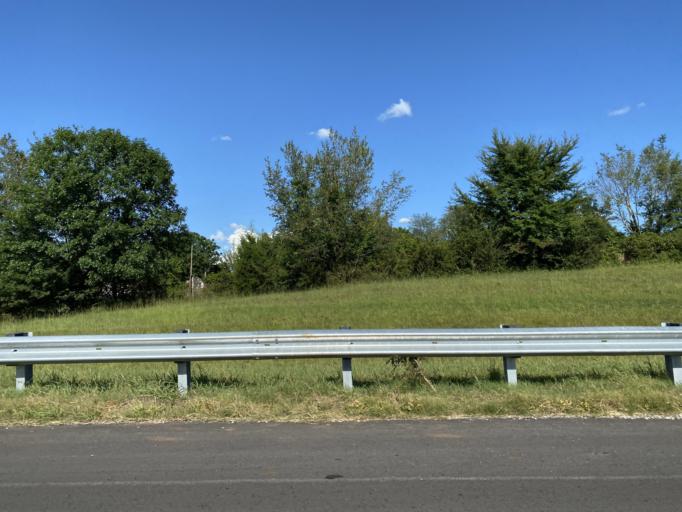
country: US
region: Alabama
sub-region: Limestone County
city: Athens
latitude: 34.7549
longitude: -86.9381
